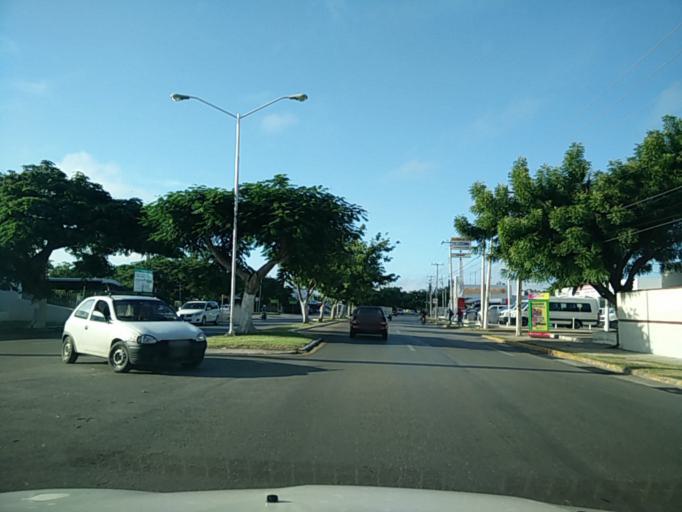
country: MX
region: Yucatan
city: Merida
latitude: 20.9549
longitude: -89.6439
